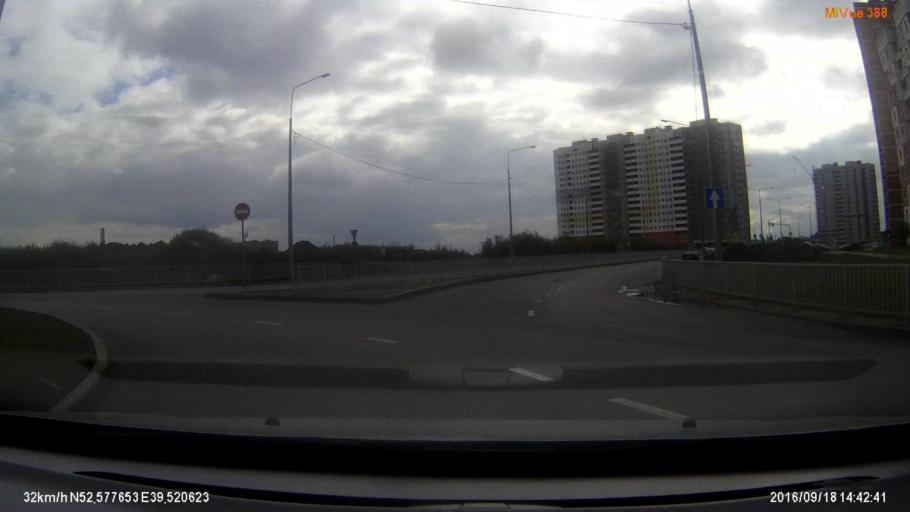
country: RU
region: Lipetsk
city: Syrskoye
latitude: 52.5777
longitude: 39.5208
